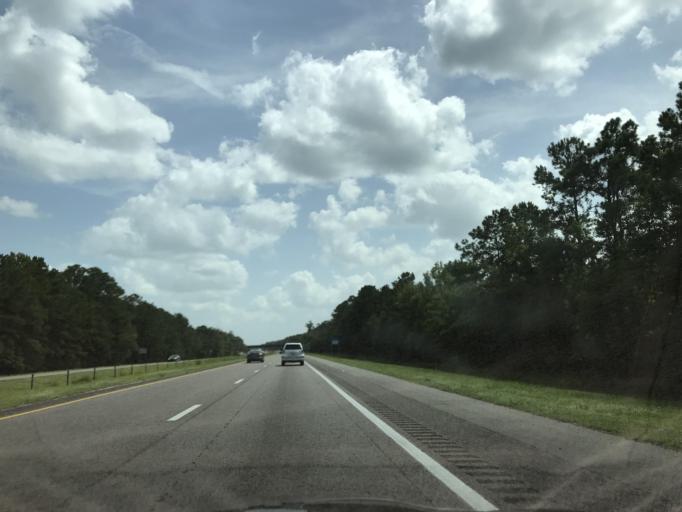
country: US
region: North Carolina
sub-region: Pender County
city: Burgaw
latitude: 34.5831
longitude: -77.9046
